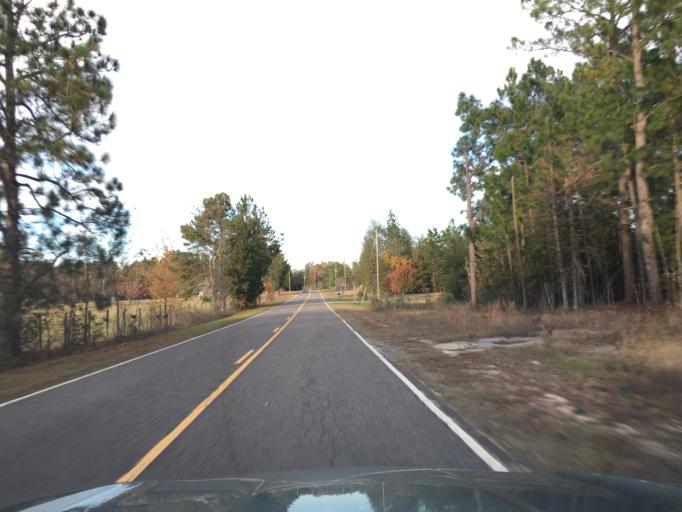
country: US
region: South Carolina
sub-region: Lexington County
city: Red Bank
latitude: 33.7017
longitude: -81.3578
